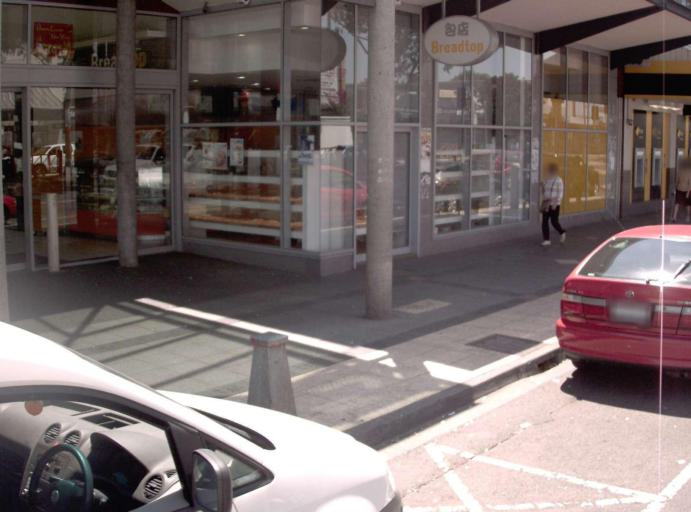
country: AU
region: Victoria
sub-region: Greater Dandenong
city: Springvale
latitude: -37.9513
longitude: 145.1524
